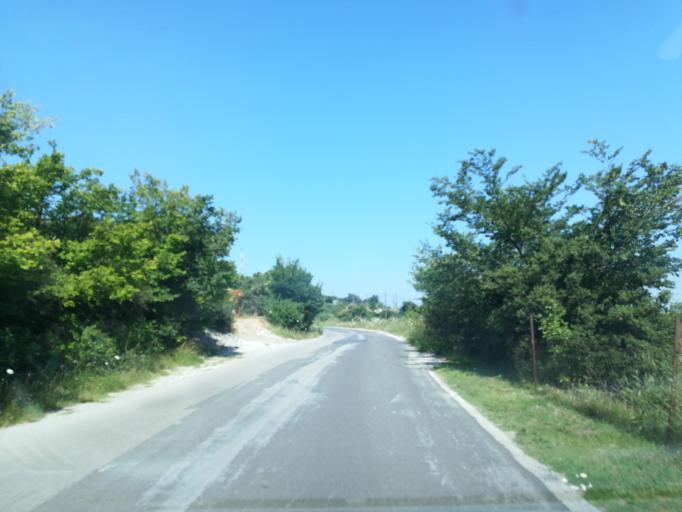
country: GR
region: Central Macedonia
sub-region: Nomos Thessalonikis
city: Asvestochori
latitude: 40.6330
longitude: 23.0259
